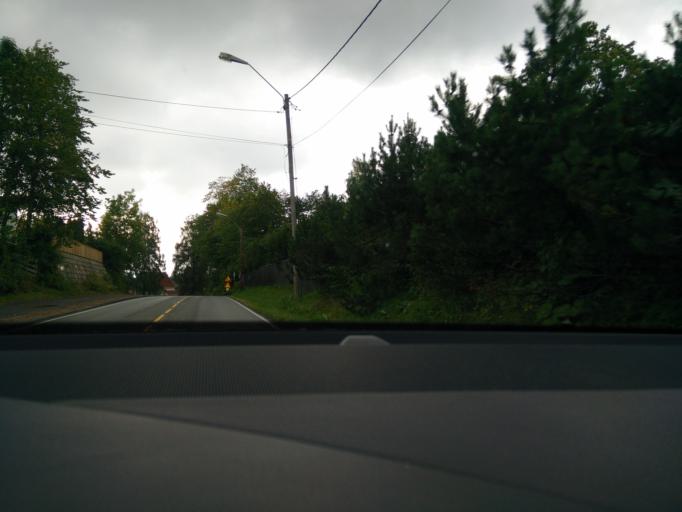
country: NO
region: Akershus
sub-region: Baerum
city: Lysaker
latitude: 59.9310
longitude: 10.6135
